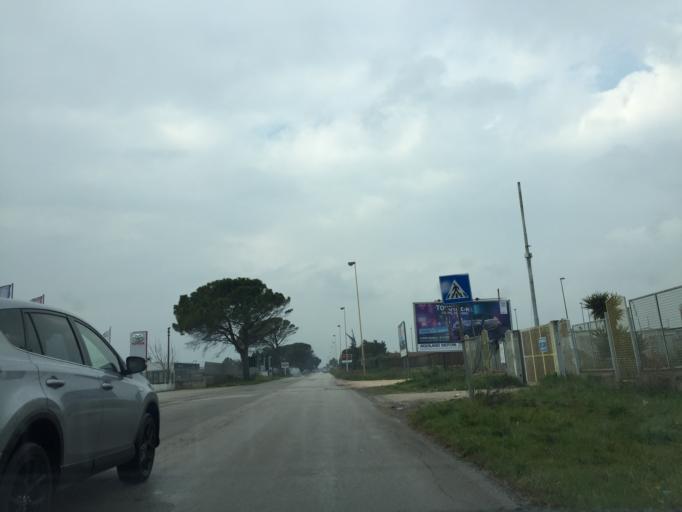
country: IT
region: Apulia
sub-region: Provincia di Foggia
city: Foggia
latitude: 41.4481
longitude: 15.5107
